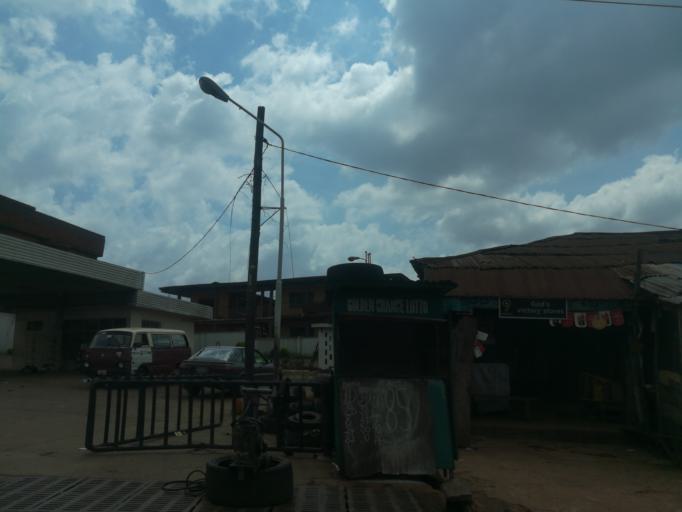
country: NG
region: Oyo
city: Ibadan
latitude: 7.3935
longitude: 3.9161
